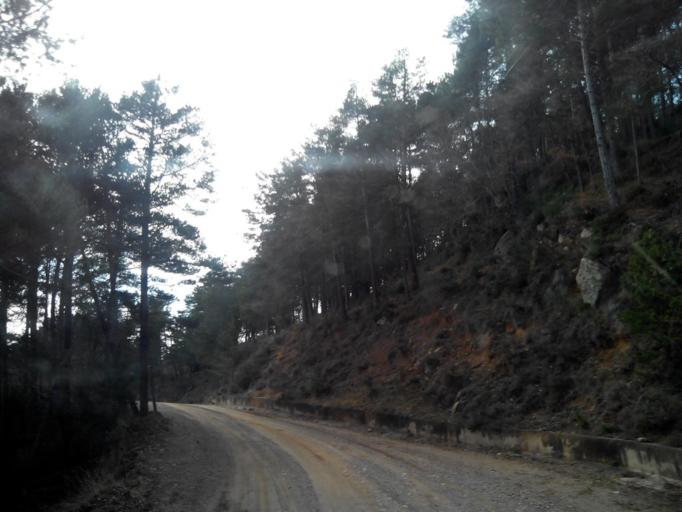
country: ES
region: Catalonia
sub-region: Provincia de Barcelona
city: Vilada
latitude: 42.1634
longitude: 1.9310
